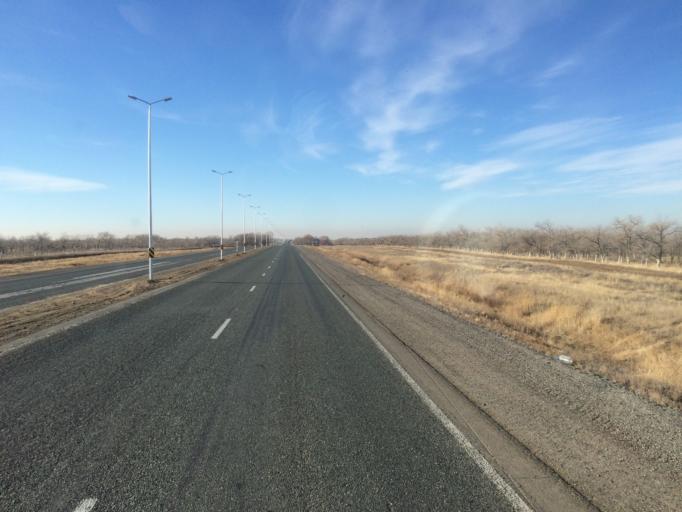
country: KZ
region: Aqtoebe
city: Aqtobe
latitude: 50.2924
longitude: 57.3825
